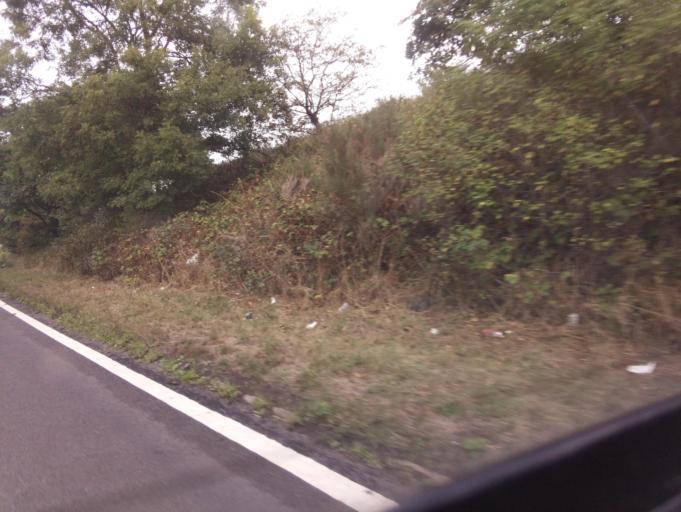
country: GB
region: England
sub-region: Shropshire
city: Bridgnorth
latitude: 52.5698
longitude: -2.3932
